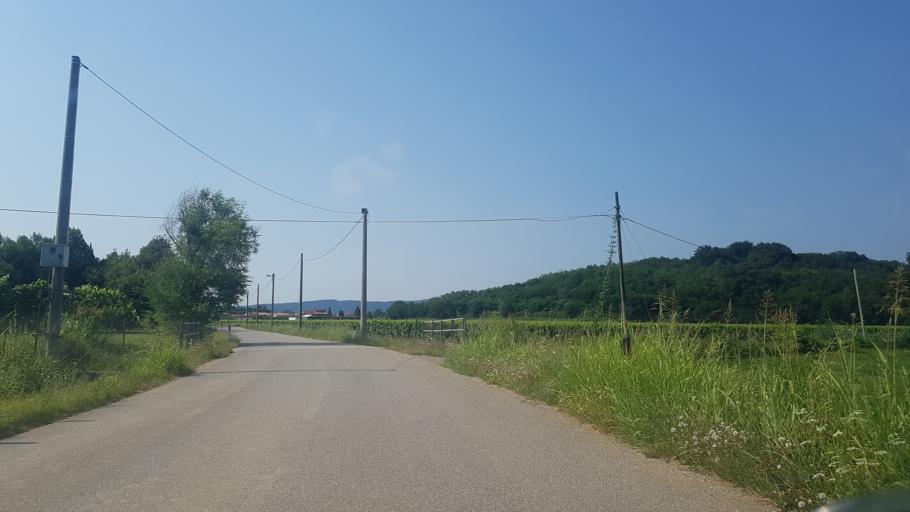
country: IT
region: Friuli Venezia Giulia
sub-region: Provincia di Gorizia
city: Mossa
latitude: 45.9452
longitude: 13.5731
